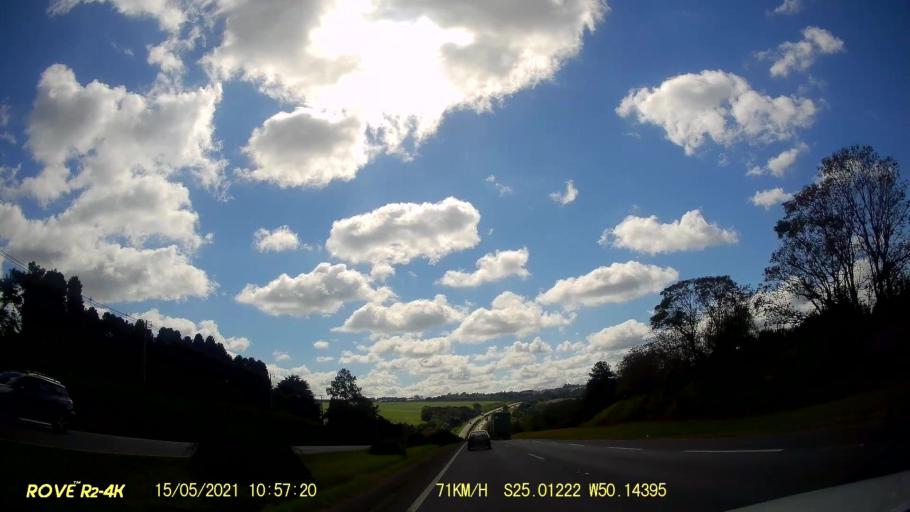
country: BR
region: Parana
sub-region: Carambei
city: Carambei
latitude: -25.0124
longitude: -50.1441
